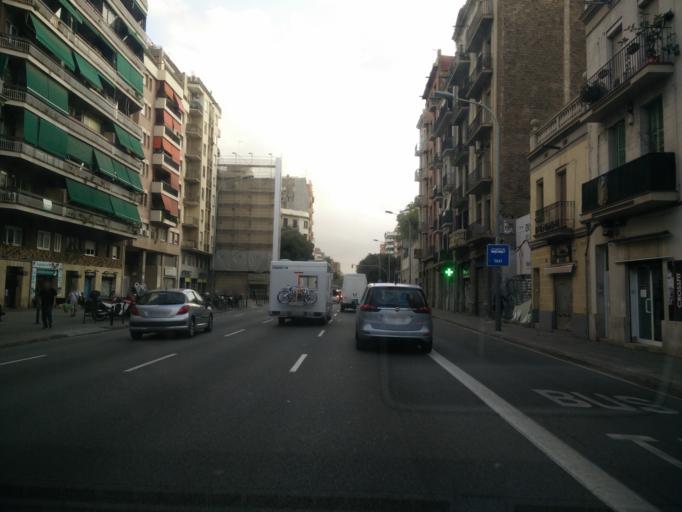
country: ES
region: Catalonia
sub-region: Provincia de Barcelona
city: Sant Marti
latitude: 41.4068
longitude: 2.1843
